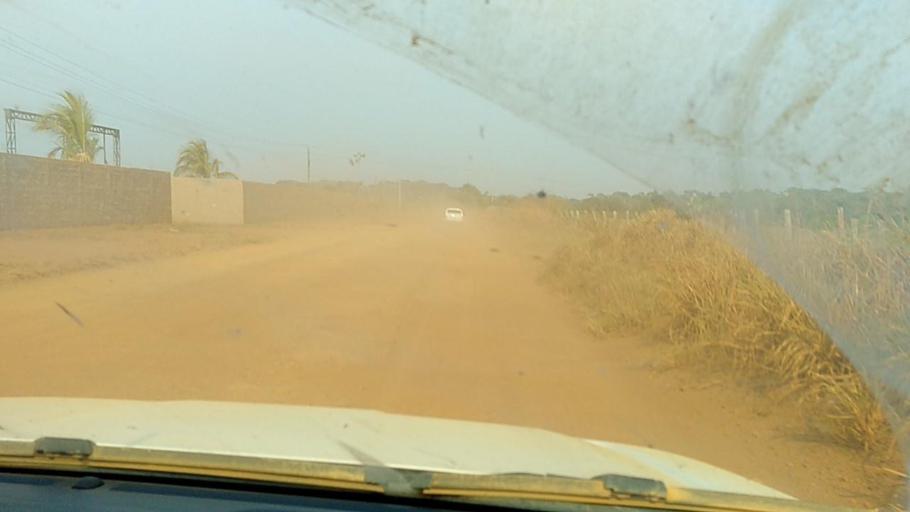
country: BR
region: Rondonia
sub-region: Porto Velho
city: Porto Velho
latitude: -8.7598
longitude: -63.9743
